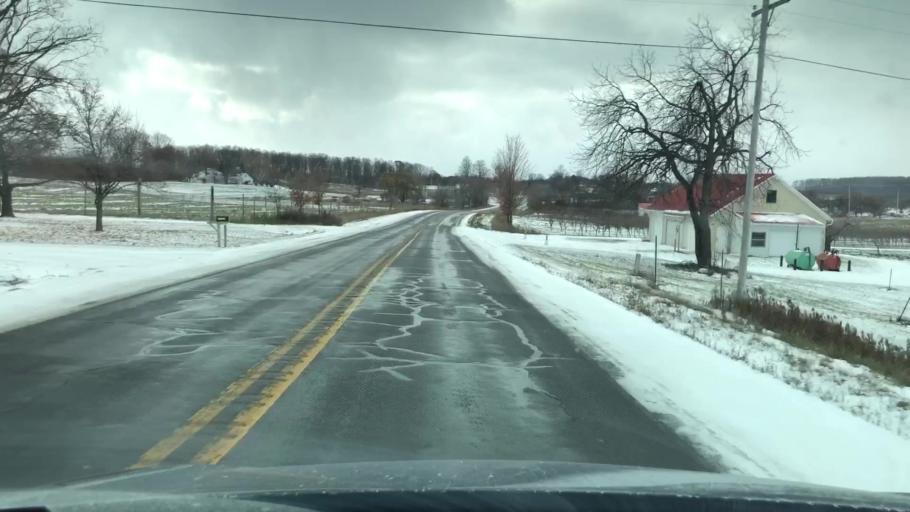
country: US
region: Michigan
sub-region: Antrim County
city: Elk Rapids
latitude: 44.8584
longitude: -85.5235
